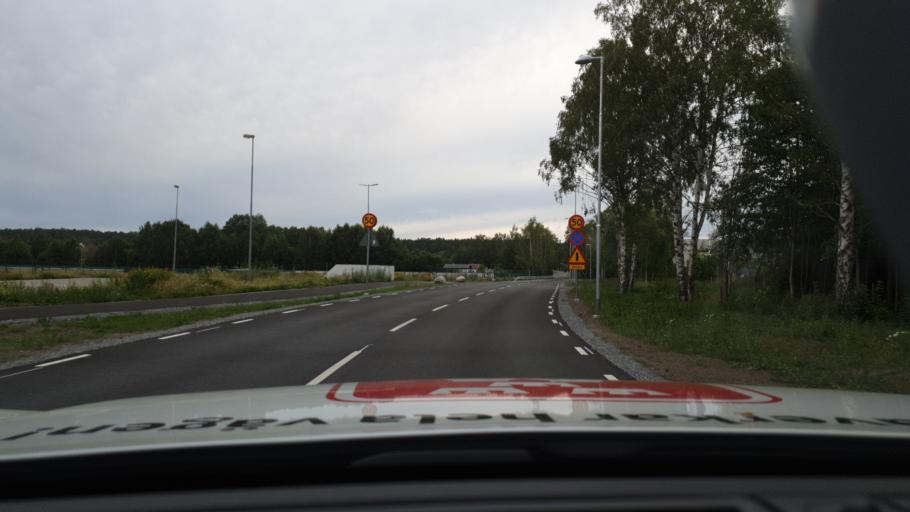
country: SE
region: Stockholm
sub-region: Osterakers Kommun
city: Akersberga
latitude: 59.4776
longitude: 18.2924
